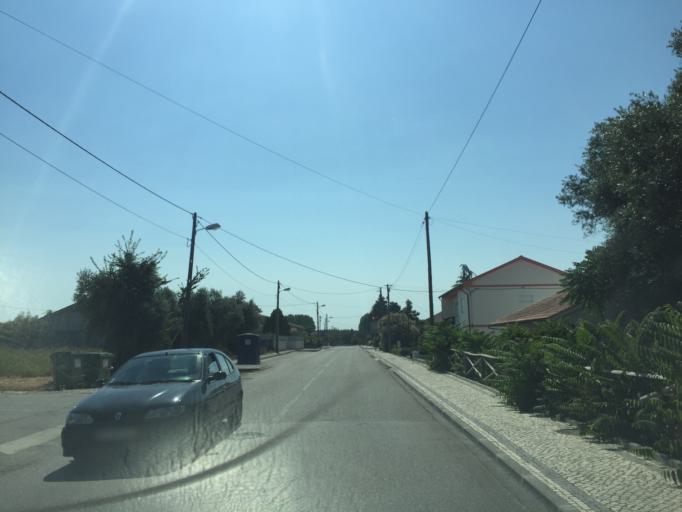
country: PT
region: Coimbra
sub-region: Cantanhede
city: Cantanhede
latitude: 40.3402
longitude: -8.6000
